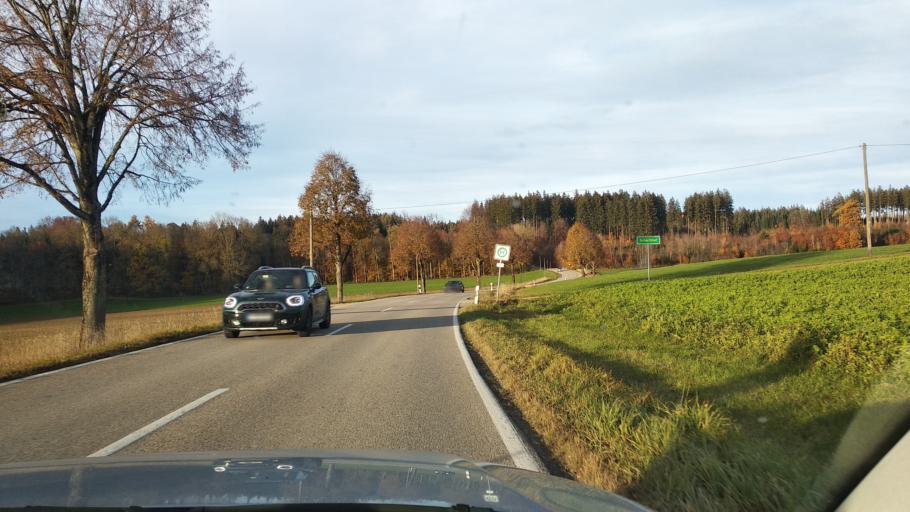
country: DE
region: Bavaria
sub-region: Upper Bavaria
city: Moosach
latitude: 48.0425
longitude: 11.8582
